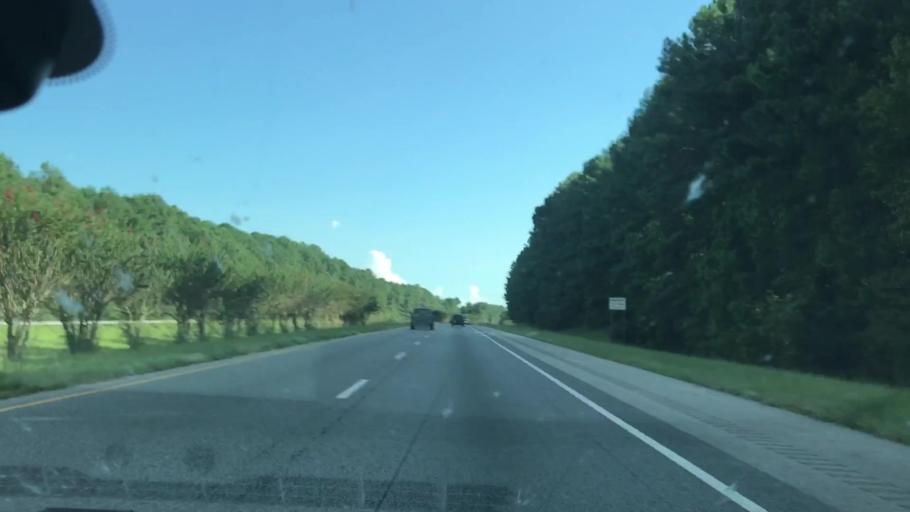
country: US
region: Georgia
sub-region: Harris County
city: Pine Mountain
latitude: 32.9260
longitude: -84.9480
